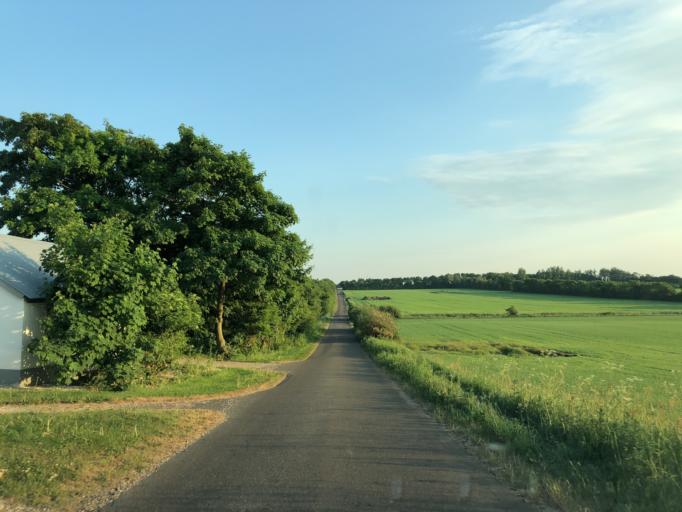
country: DK
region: Central Jutland
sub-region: Struer Kommune
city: Struer
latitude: 56.4012
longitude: 8.4859
